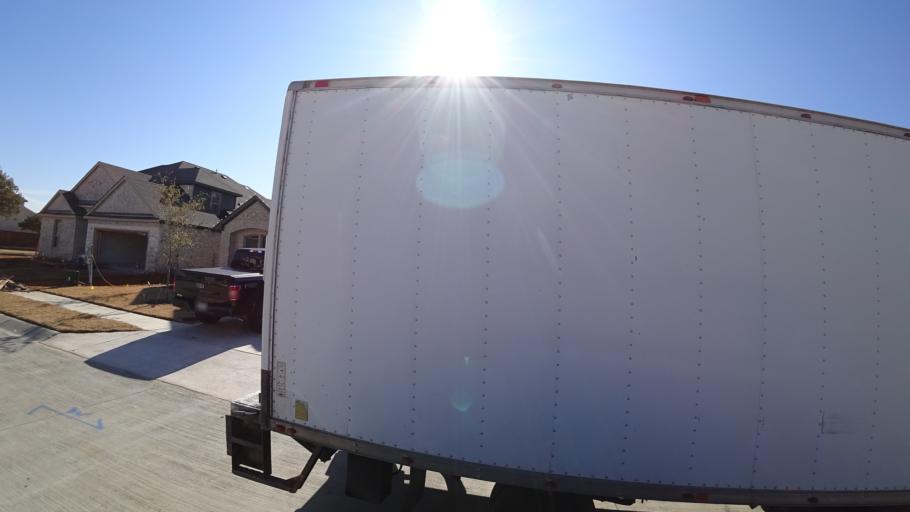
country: US
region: Texas
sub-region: Denton County
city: Lewisville
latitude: 33.0071
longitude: -97.0146
